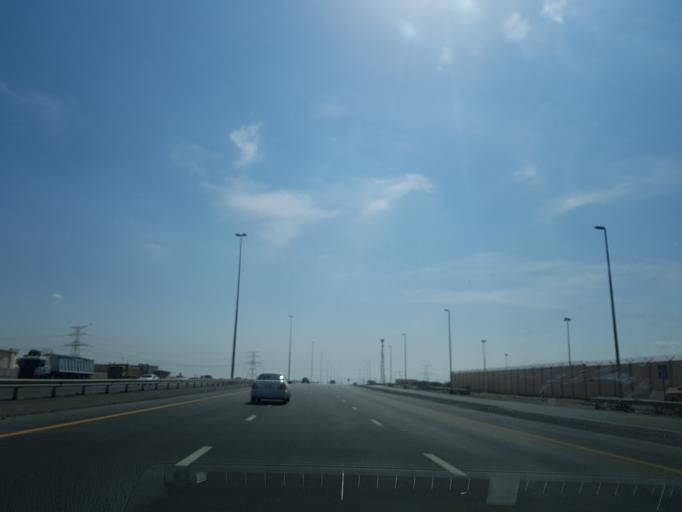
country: AE
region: Ra's al Khaymah
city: Ras al-Khaimah
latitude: 25.7752
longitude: 56.0290
